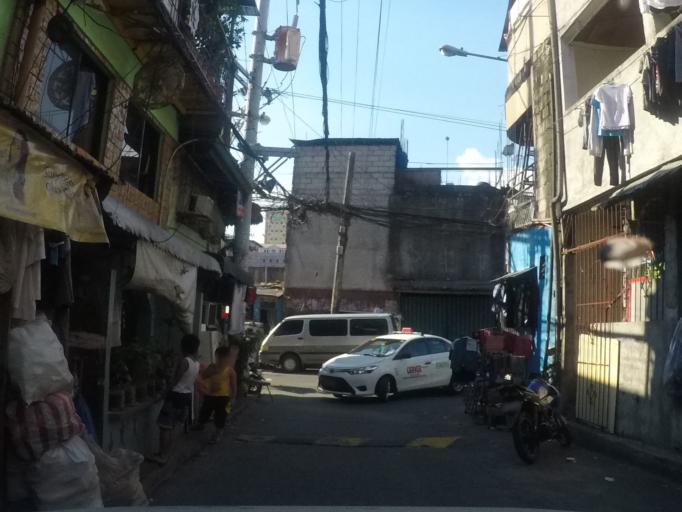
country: PH
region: Metro Manila
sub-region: San Juan
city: San Juan
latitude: 14.6068
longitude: 121.0494
